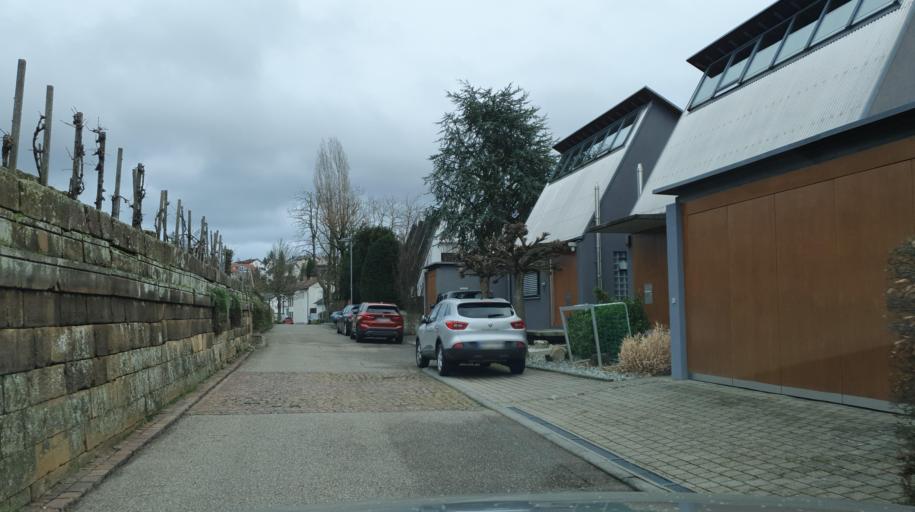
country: DE
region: Baden-Wuerttemberg
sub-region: Regierungsbezirk Stuttgart
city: Heilbronn
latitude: 49.1458
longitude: 9.2400
